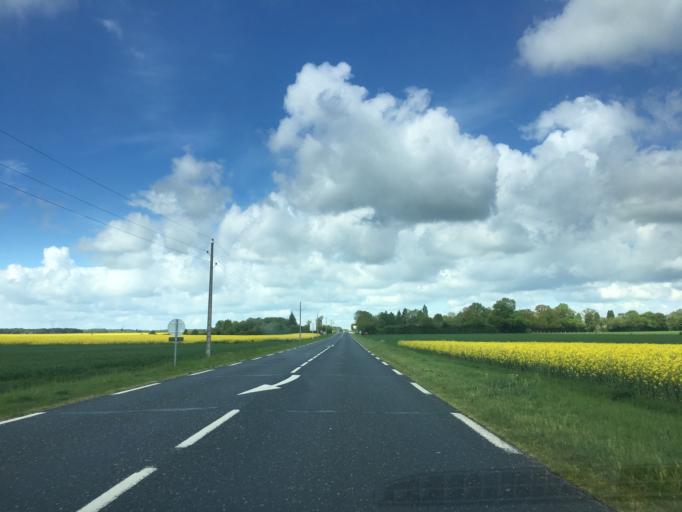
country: FR
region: Haute-Normandie
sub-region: Departement de l'Eure
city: Bourth
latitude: 48.7462
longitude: 0.8164
